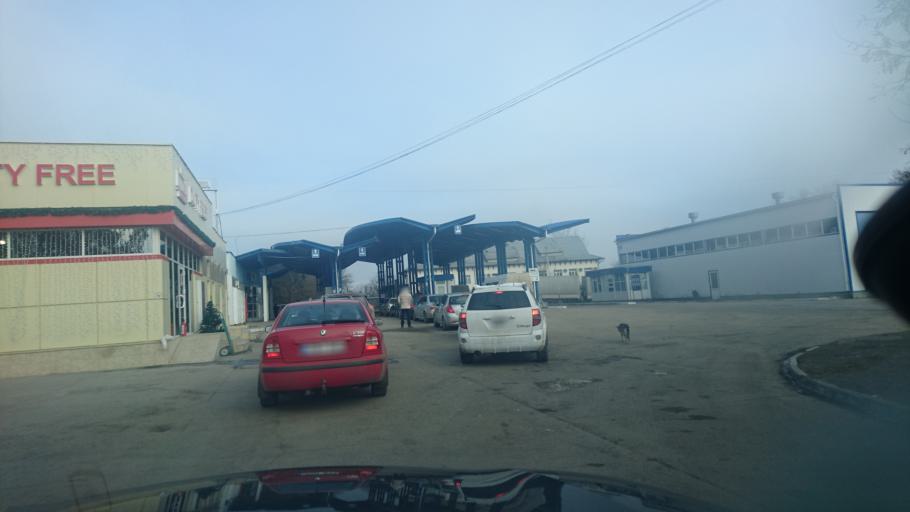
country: RO
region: Botosani
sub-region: Comuna Paltinis
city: Paltinis
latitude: 48.2653
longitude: 26.6263
